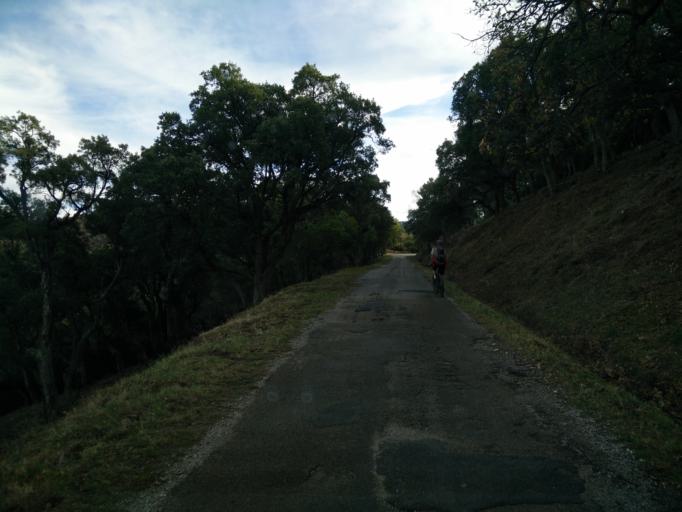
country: FR
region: Provence-Alpes-Cote d'Azur
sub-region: Departement du Var
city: Roquebrune-sur-Argens
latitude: 43.4198
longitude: 6.6381
